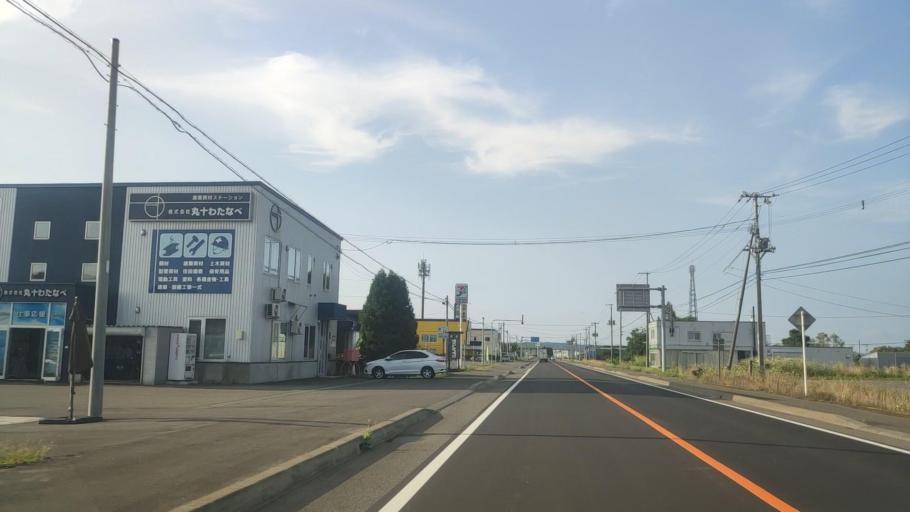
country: JP
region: Hokkaido
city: Iwamizawa
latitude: 43.0109
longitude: 141.7891
